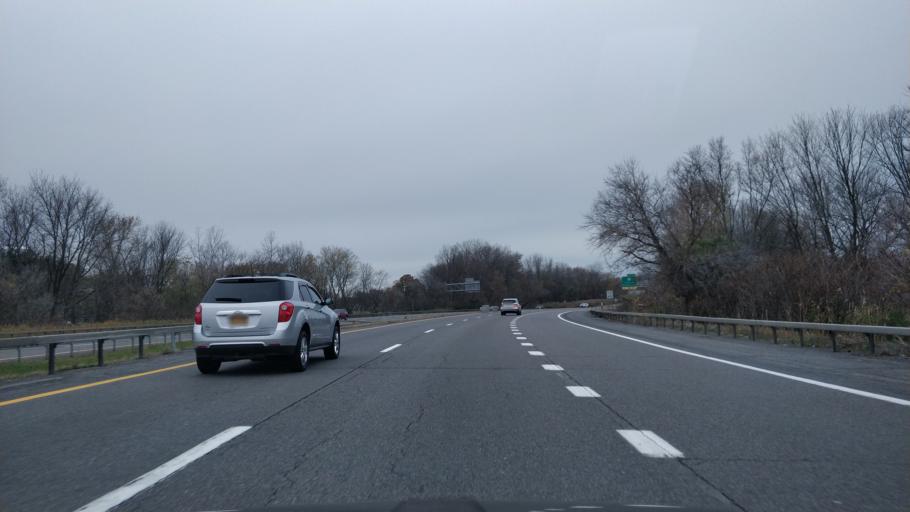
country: US
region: New York
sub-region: Onondaga County
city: North Syracuse
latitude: 43.1425
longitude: -76.1181
